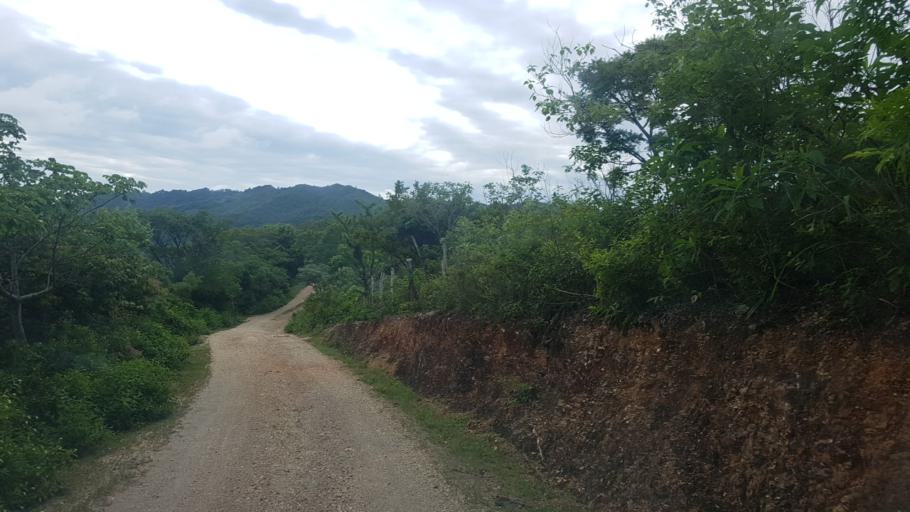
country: NI
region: Nueva Segovia
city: Mozonte
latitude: 13.5919
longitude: -86.4137
